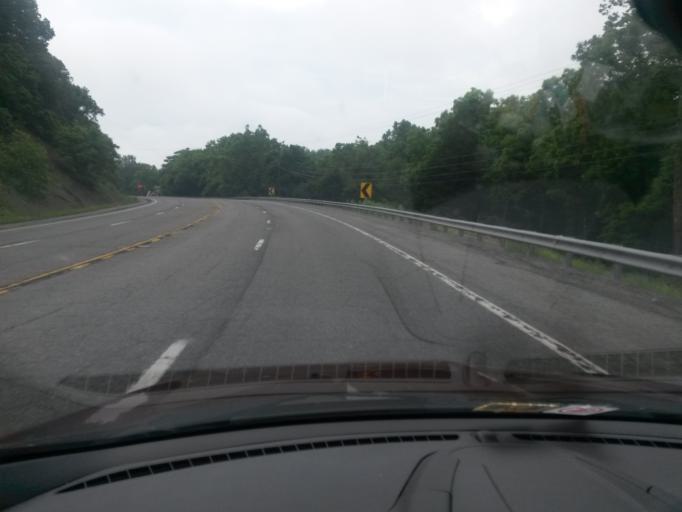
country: US
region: Virginia
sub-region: Botetourt County
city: Fincastle
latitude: 37.5110
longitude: -79.8803
